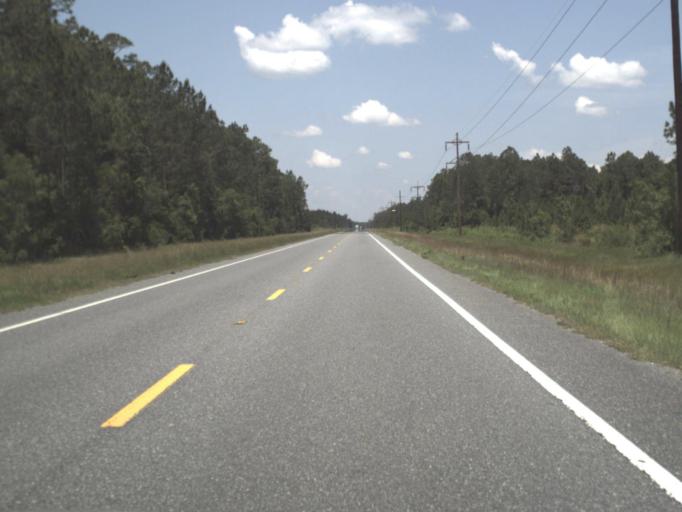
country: US
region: Florida
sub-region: Bradford County
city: Starke
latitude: 29.9749
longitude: -82.2208
